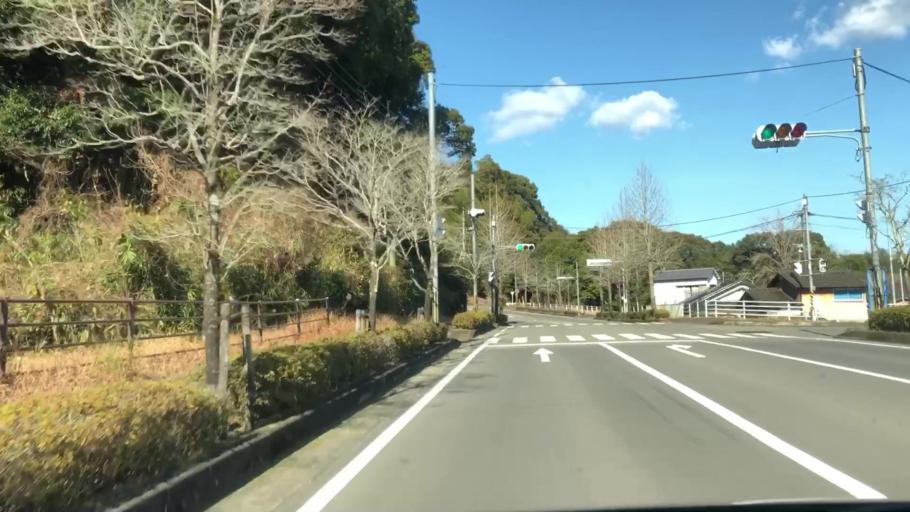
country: JP
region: Kagoshima
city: Satsumasendai
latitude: 31.8267
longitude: 130.4349
